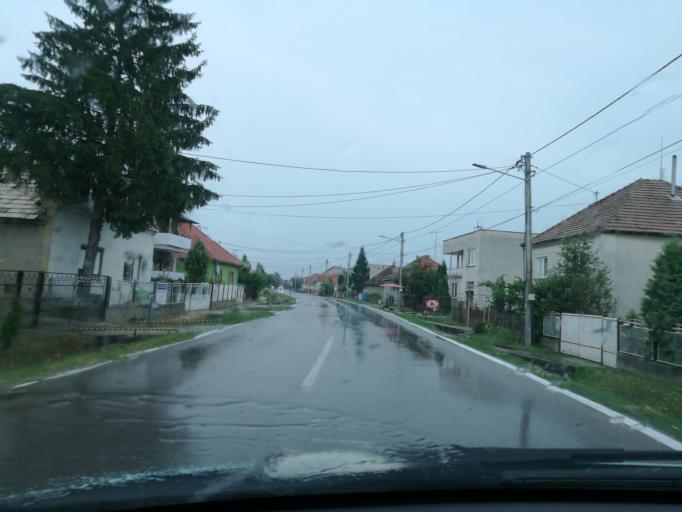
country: HU
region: Komarom-Esztergom
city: Almasfuzito
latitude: 47.7550
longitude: 18.2114
